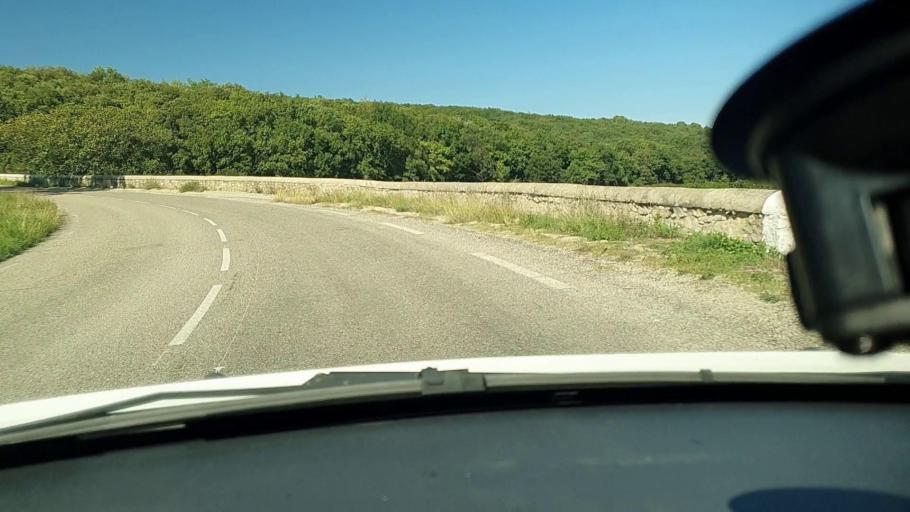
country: FR
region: Languedoc-Roussillon
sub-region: Departement du Gard
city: Saint-Paulet-de-Caisson
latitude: 44.2459
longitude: 4.5775
